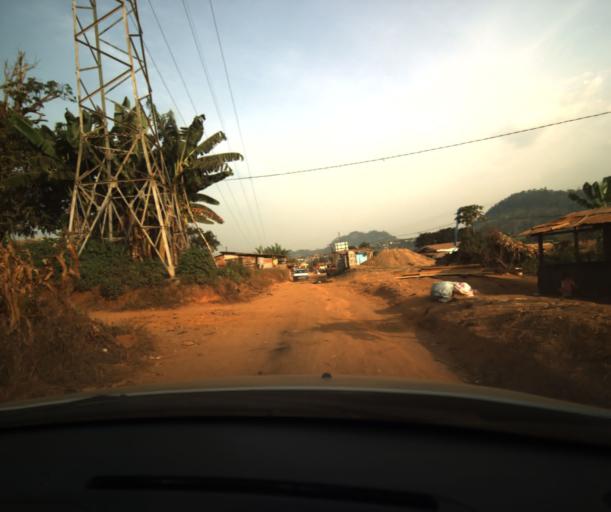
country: CM
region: Centre
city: Yaounde
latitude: 3.8752
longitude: 11.4306
